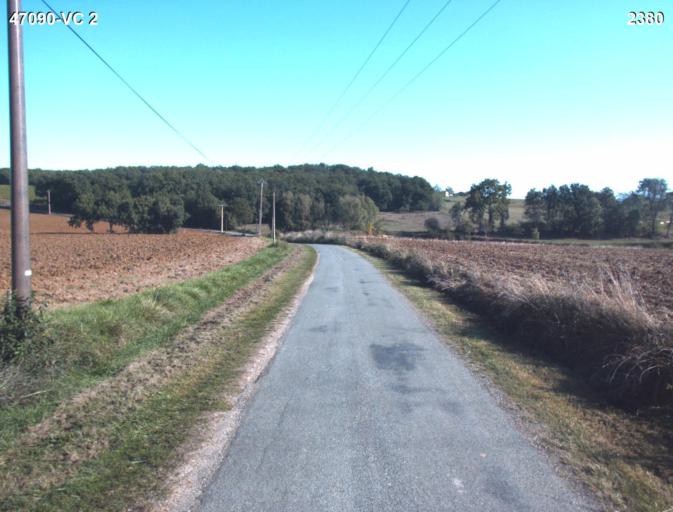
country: FR
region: Aquitaine
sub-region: Departement du Lot-et-Garonne
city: Nerac
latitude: 44.1738
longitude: 0.3763
